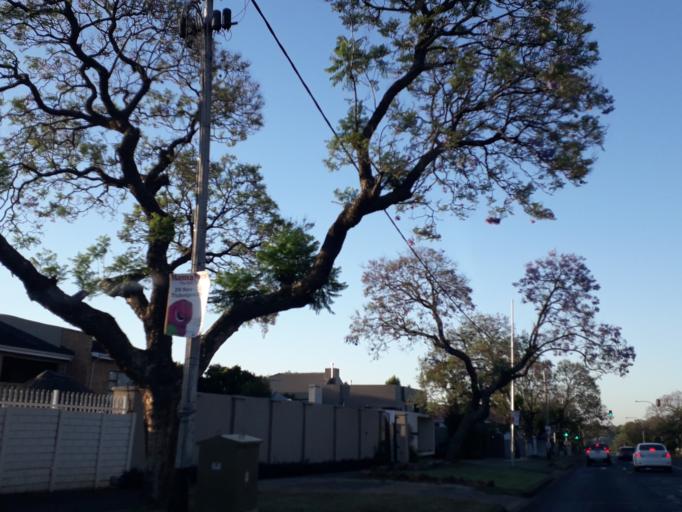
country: ZA
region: Gauteng
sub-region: City of Johannesburg Metropolitan Municipality
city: Johannesburg
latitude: -26.1527
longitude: 28.0103
